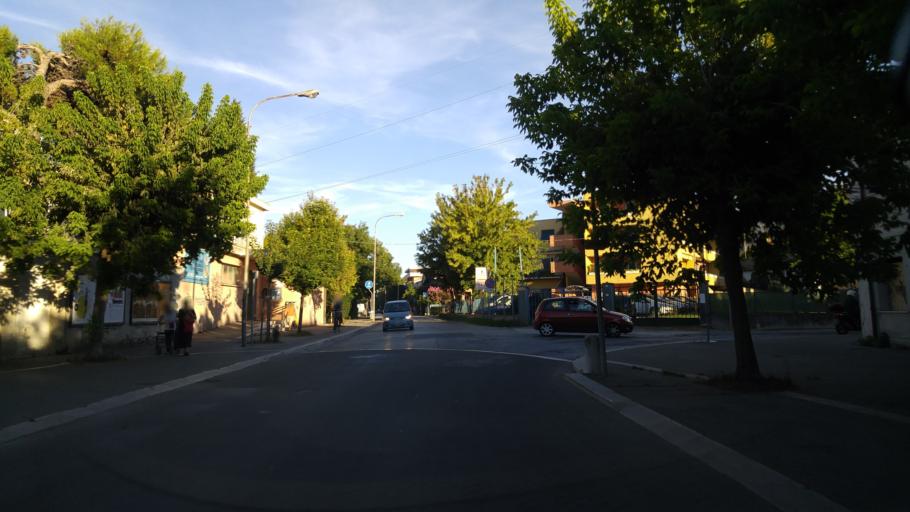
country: IT
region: The Marches
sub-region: Provincia di Pesaro e Urbino
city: Fano
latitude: 43.8355
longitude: 13.0241
